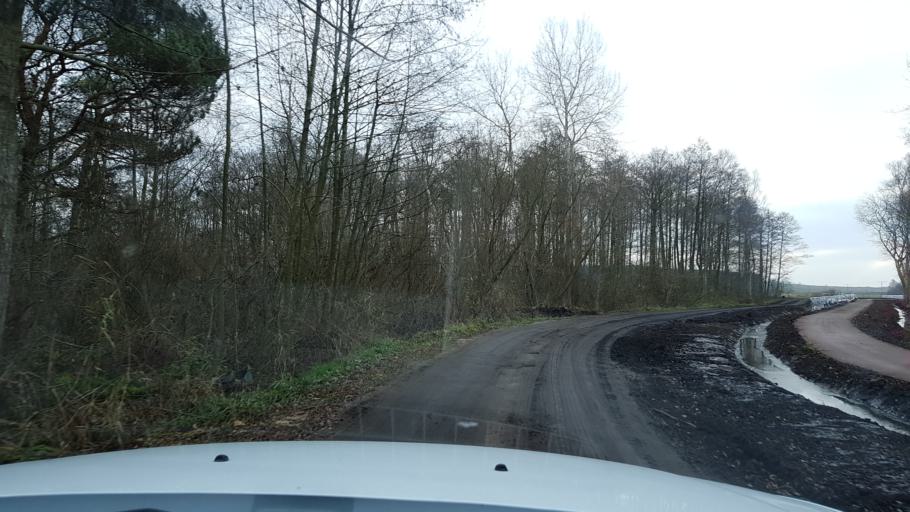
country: PL
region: West Pomeranian Voivodeship
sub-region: Powiat kolobrzeski
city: Grzybowo
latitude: 54.1313
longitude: 15.5158
